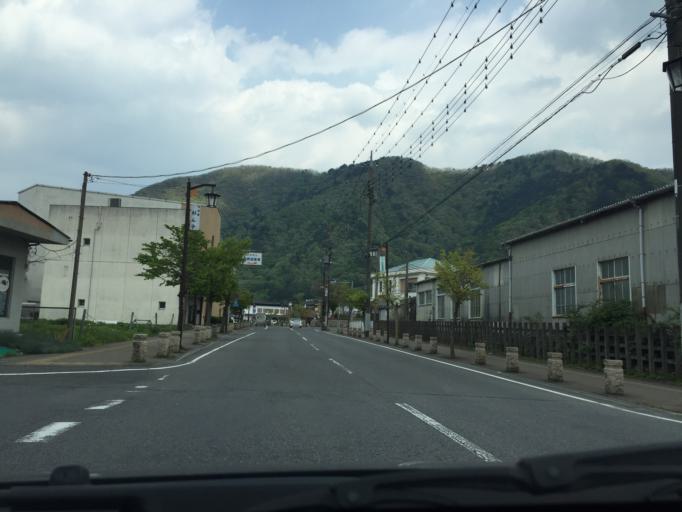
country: JP
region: Tochigi
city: Imaichi
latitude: 36.8228
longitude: 139.7149
